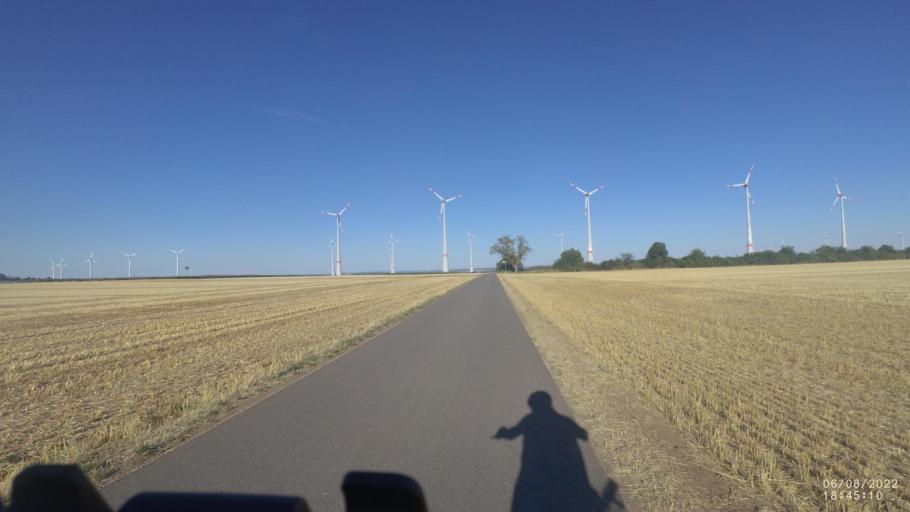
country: DE
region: Rheinland-Pfalz
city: Worrstadt
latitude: 49.8311
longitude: 8.1278
